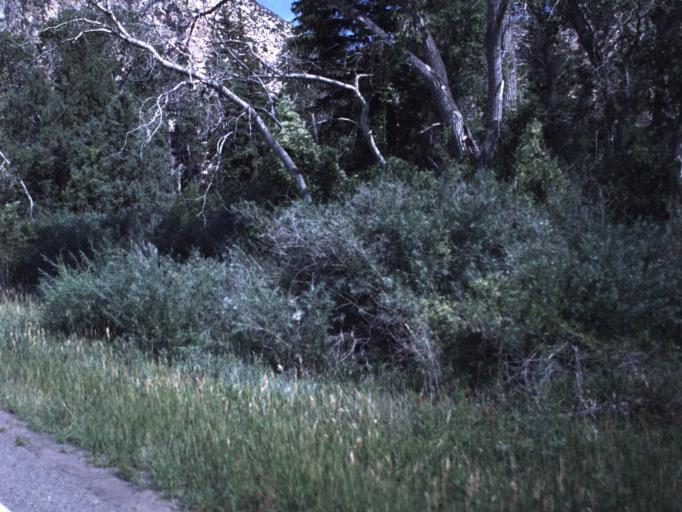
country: US
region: Utah
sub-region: Daggett County
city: Manila
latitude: 40.9268
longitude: -109.7191
